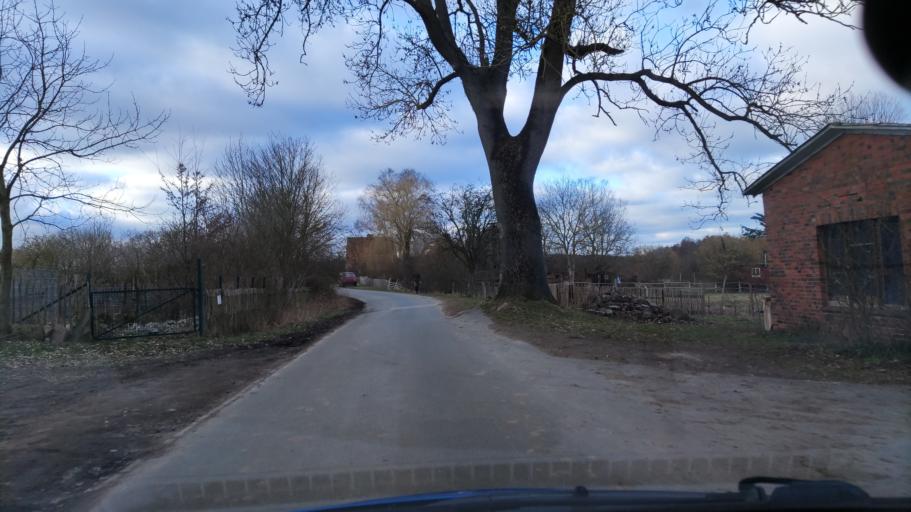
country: DE
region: Lower Saxony
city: Gohrde
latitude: 53.1593
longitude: 10.8795
